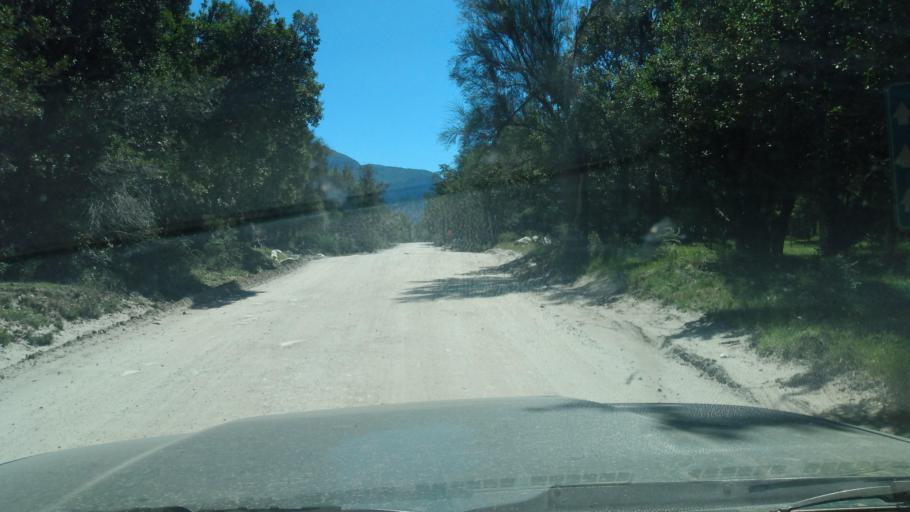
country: AR
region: Neuquen
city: Villa La Angostura
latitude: -40.6150
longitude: -71.5487
